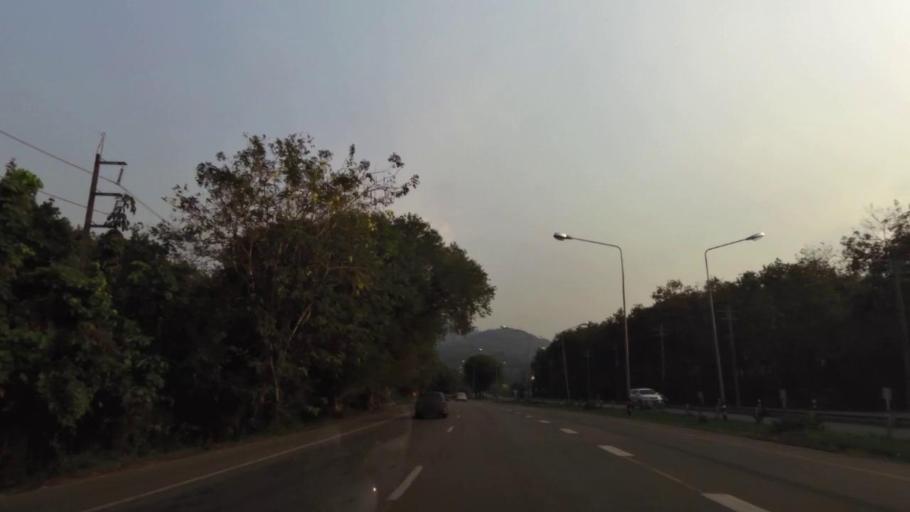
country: TH
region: Chanthaburi
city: Chanthaburi
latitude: 12.5765
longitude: 102.1606
